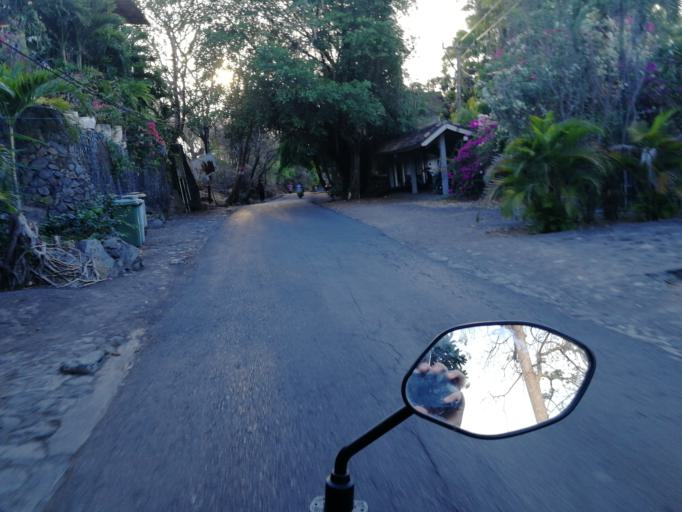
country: ID
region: Bali
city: Biaslantang Kaler
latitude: -8.3351
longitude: 115.6545
